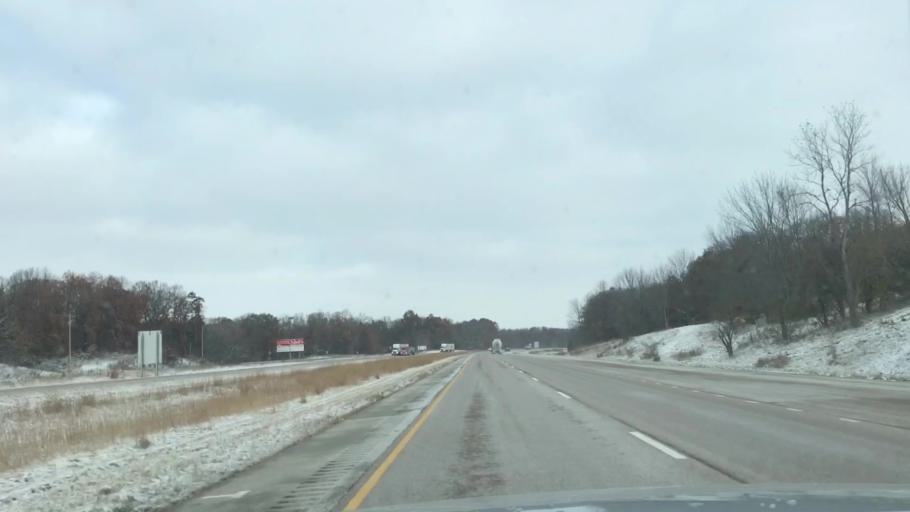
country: US
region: Illinois
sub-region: Macoupin County
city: Mount Olive
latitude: 39.0762
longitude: -89.7555
